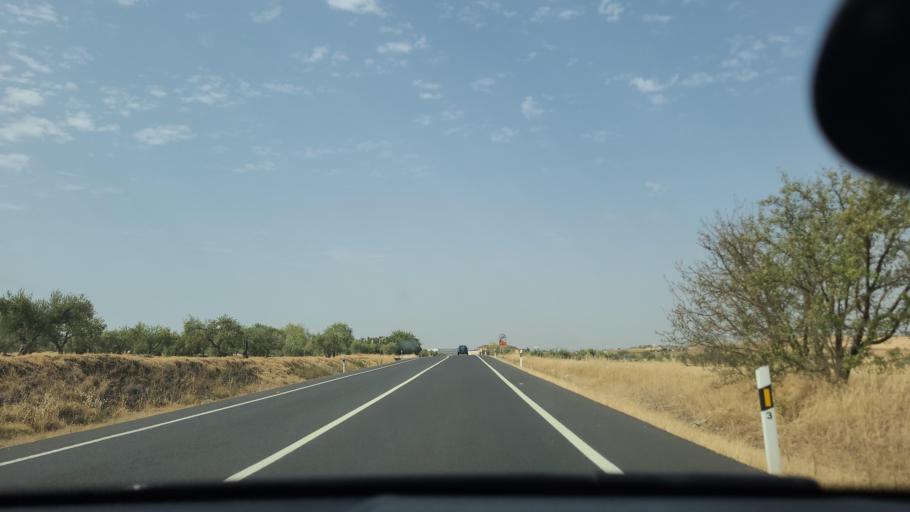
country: ES
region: Extremadura
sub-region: Provincia de Badajoz
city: Azuaga
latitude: 38.2673
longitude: -5.6900
